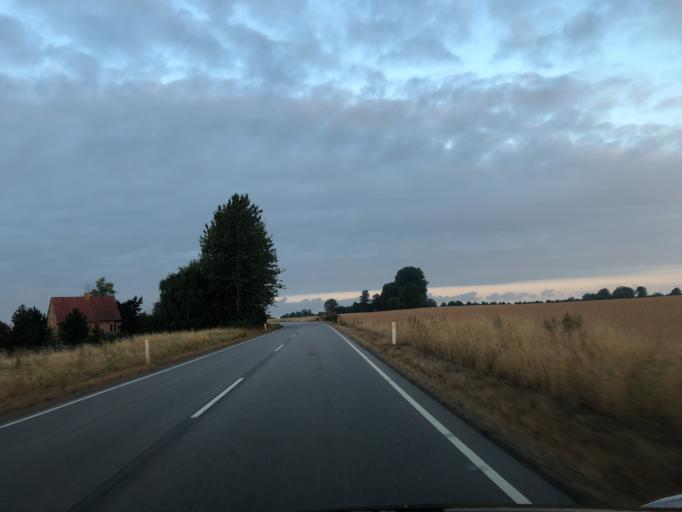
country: DK
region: Zealand
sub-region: Soro Kommune
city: Dianalund
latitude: 55.4775
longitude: 11.4900
